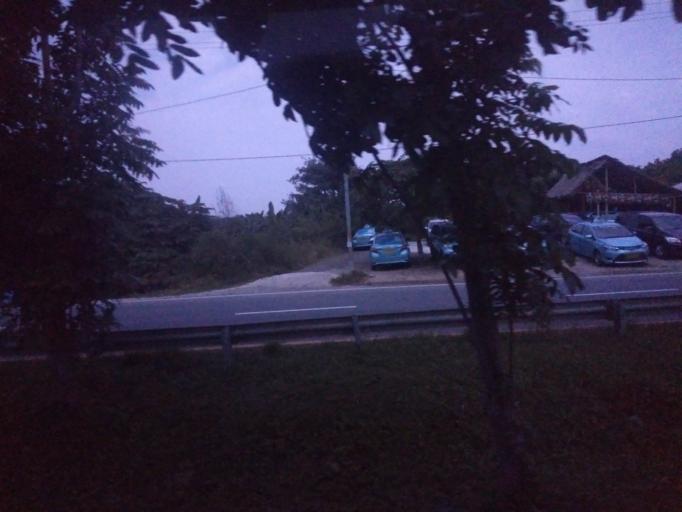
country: ID
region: North Sumatra
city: Percut
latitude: 3.5989
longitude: 98.8348
